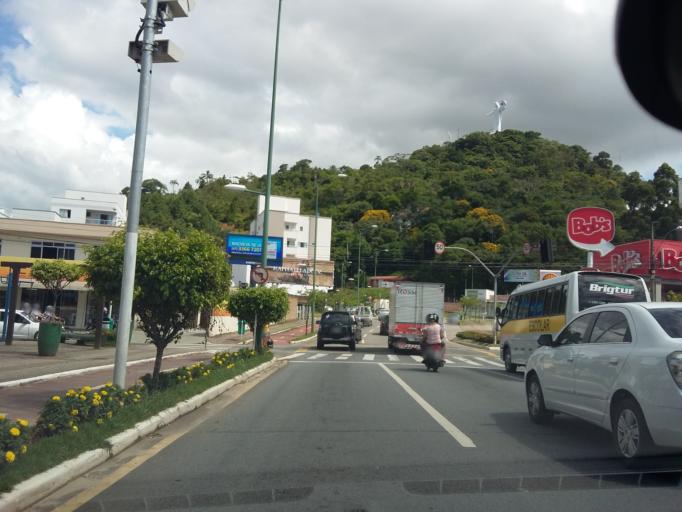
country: BR
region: Santa Catarina
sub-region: Balneario Camboriu
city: Balneario Camboriu
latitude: -26.9821
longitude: -48.6428
